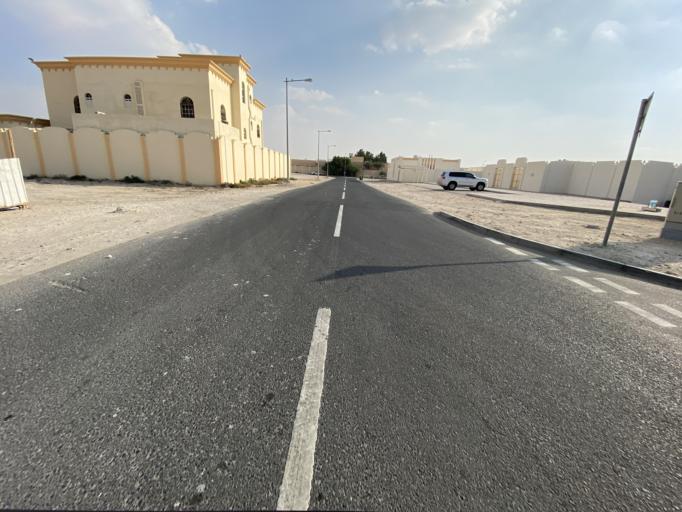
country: QA
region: Baladiyat ar Rayyan
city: Ar Rayyan
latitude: 25.2364
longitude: 51.3787
